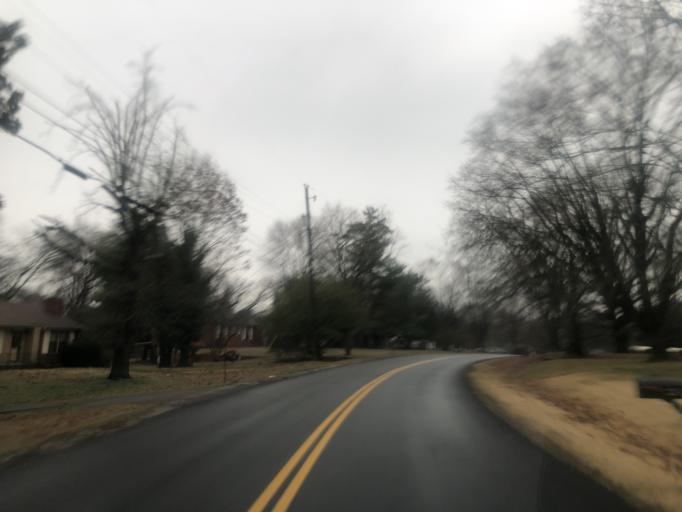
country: US
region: Tennessee
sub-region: Davidson County
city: Lakewood
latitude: 36.1655
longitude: -86.6827
